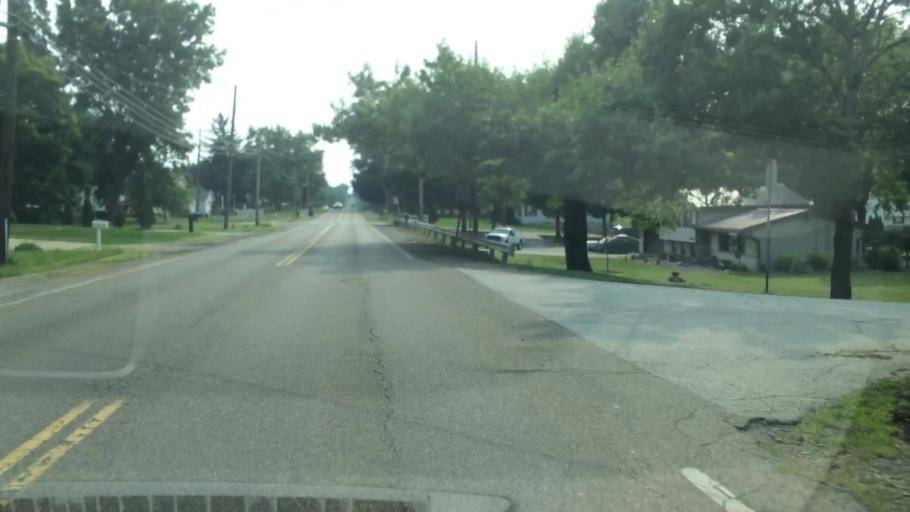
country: US
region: Ohio
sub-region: Summit County
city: Tallmadge
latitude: 41.0931
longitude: -81.4544
